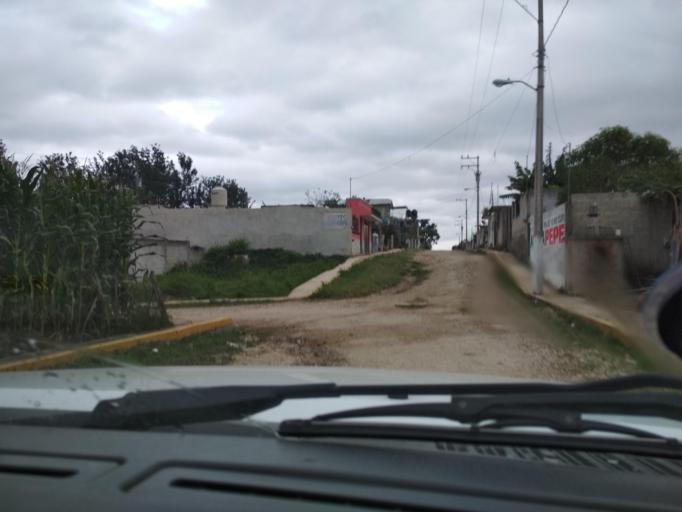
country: MX
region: Veracruz
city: El Castillo
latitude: 19.5714
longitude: -96.8497
